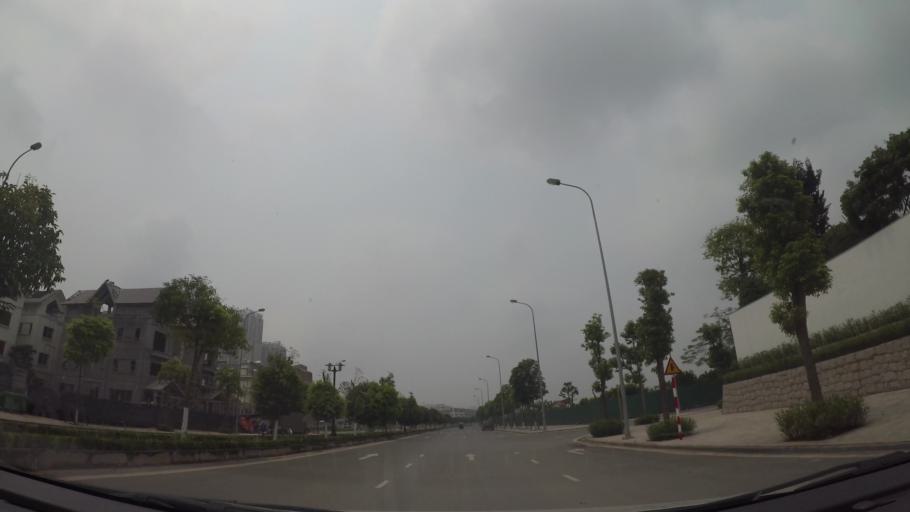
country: VN
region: Ha Noi
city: Ha Dong
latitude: 20.9781
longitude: 105.7584
